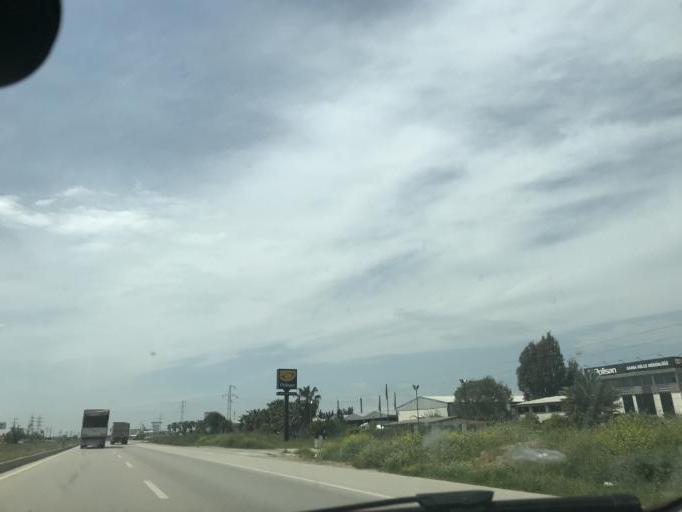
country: TR
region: Adana
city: Yuregir
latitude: 36.9785
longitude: 35.4641
